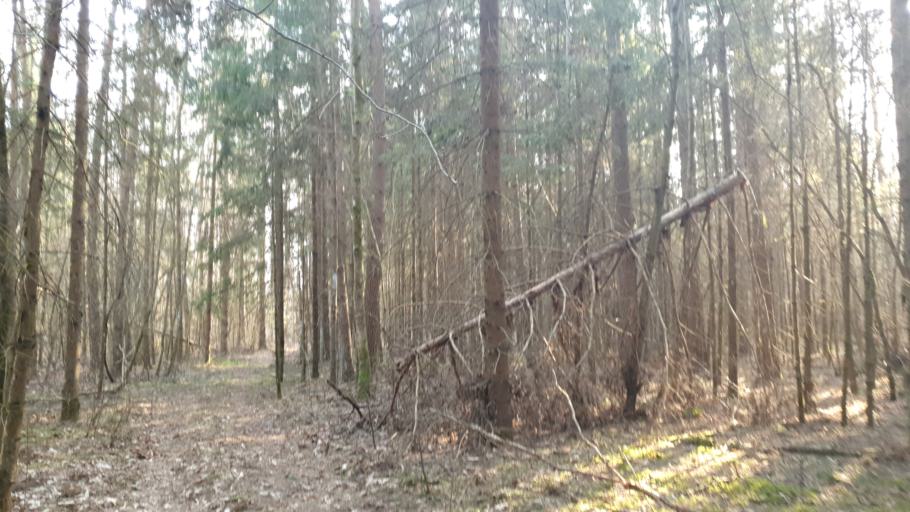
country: LT
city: Nemencine
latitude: 54.8739
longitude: 25.5714
